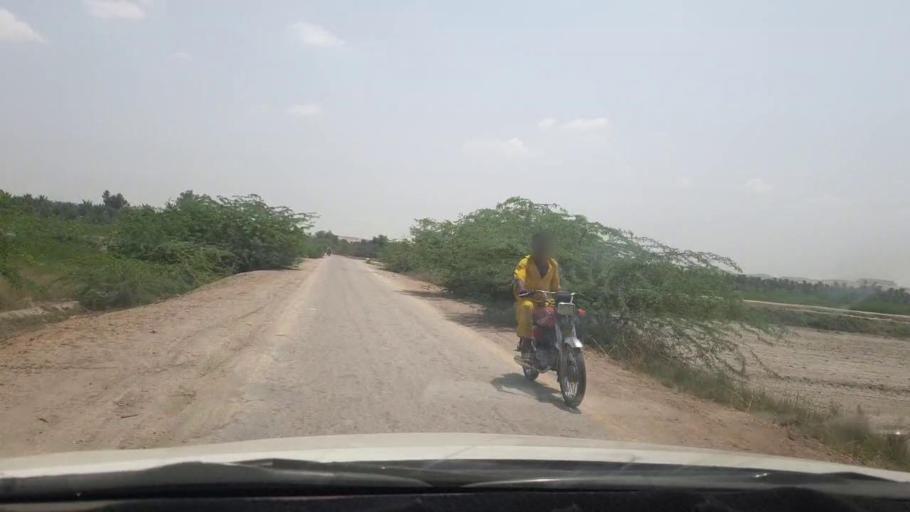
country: PK
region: Sindh
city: Khairpur
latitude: 27.5346
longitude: 68.8894
